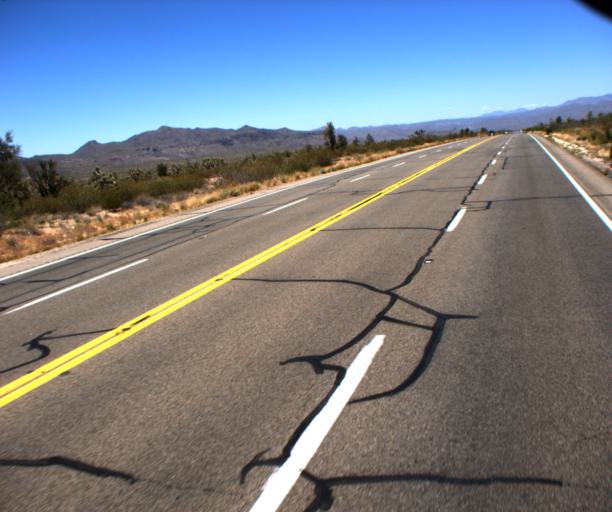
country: US
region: Arizona
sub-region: Yavapai County
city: Congress
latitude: 34.2768
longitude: -113.0993
